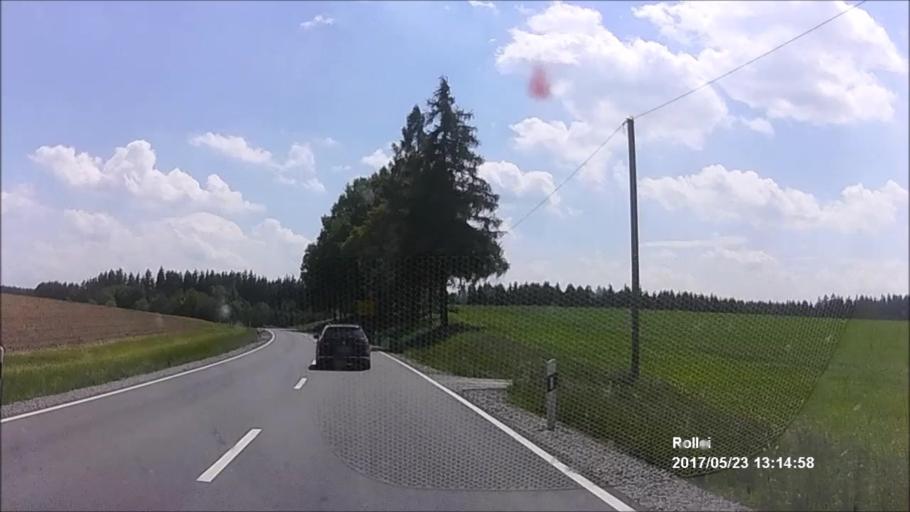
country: DE
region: Bavaria
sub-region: Upper Bavaria
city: Hohenpolding
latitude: 48.4083
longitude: 12.1258
